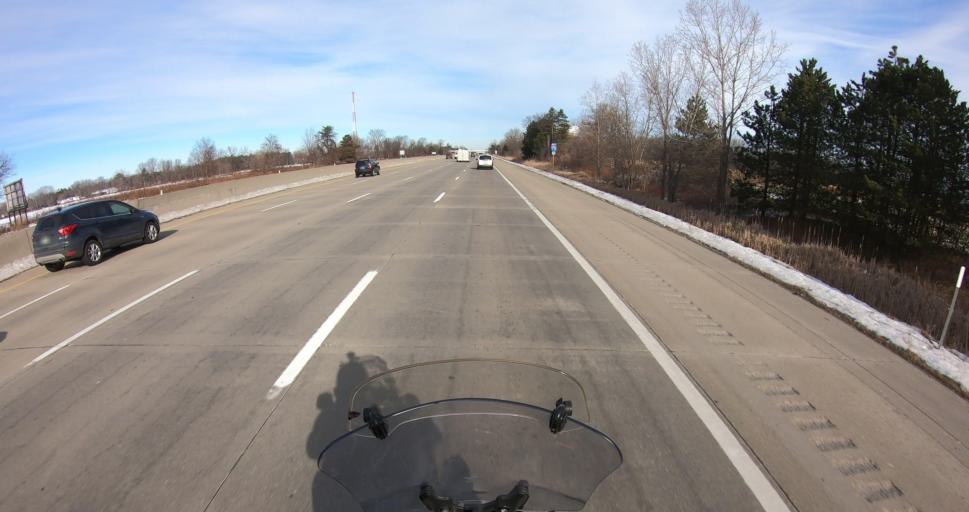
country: US
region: Michigan
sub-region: Genesee County
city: Clio
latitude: 43.1888
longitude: -83.7672
